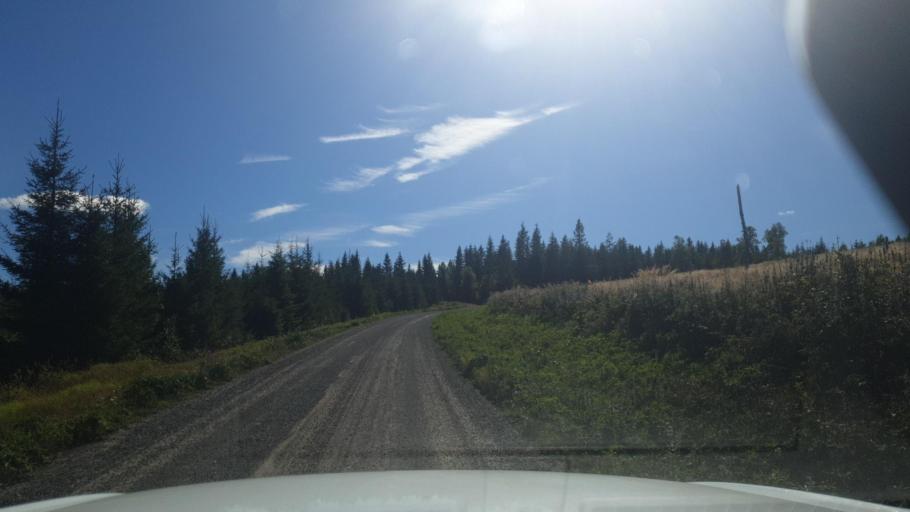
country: SE
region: Vaermland
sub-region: Torsby Kommun
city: Torsby
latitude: 60.1758
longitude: 12.6464
